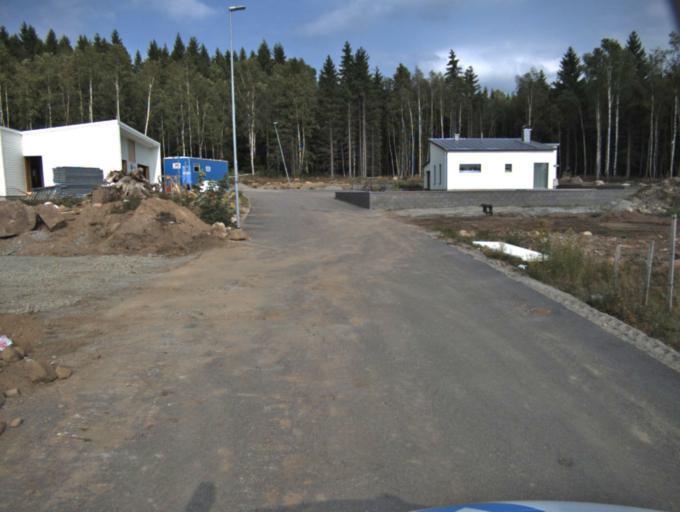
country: SE
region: Vaestra Goetaland
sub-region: Ulricehamns Kommun
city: Ulricehamn
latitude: 57.7798
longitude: 13.4318
